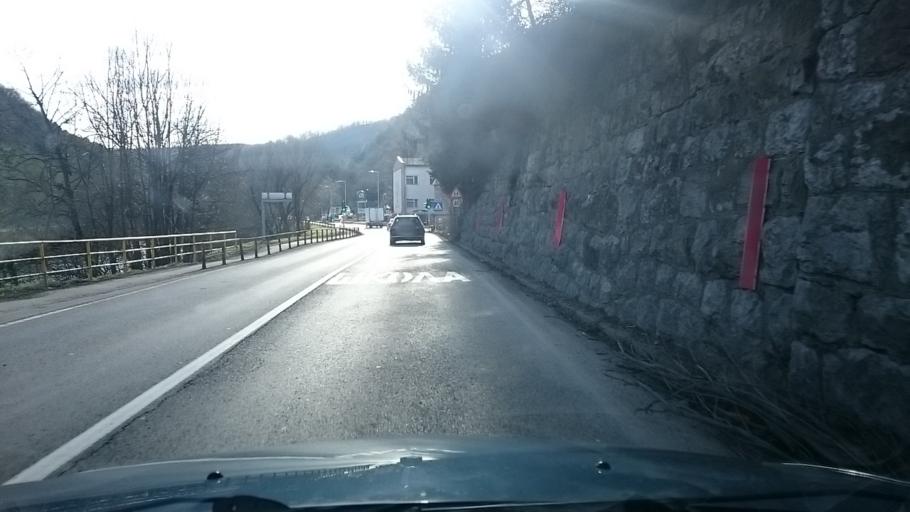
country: BA
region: Republika Srpska
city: Hiseti
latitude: 44.7483
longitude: 17.1563
